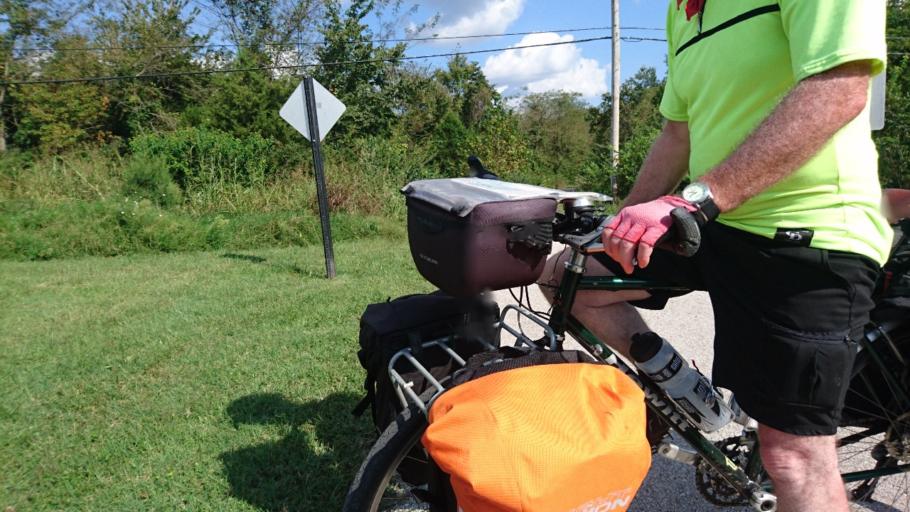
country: US
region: Missouri
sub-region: Saint Louis County
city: Eureka
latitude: 38.5469
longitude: -90.6298
